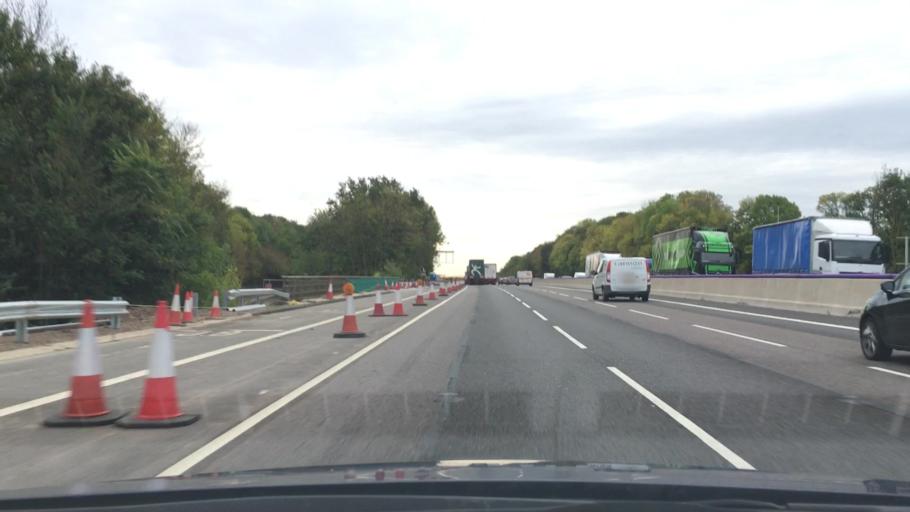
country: GB
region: England
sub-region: Northamptonshire
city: Long Buckby
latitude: 52.3269
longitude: -1.1426
